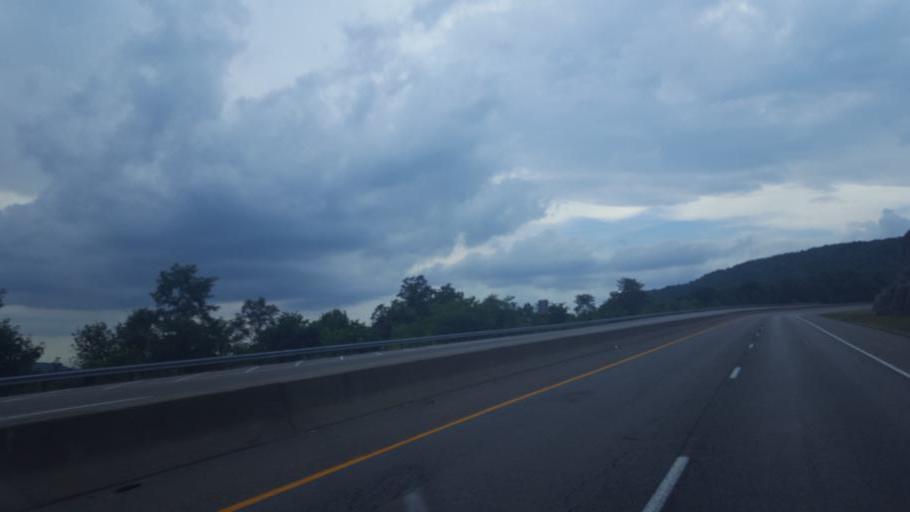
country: US
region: Kentucky
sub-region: Letcher County
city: Jenkins
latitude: 37.1577
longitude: -82.6423
